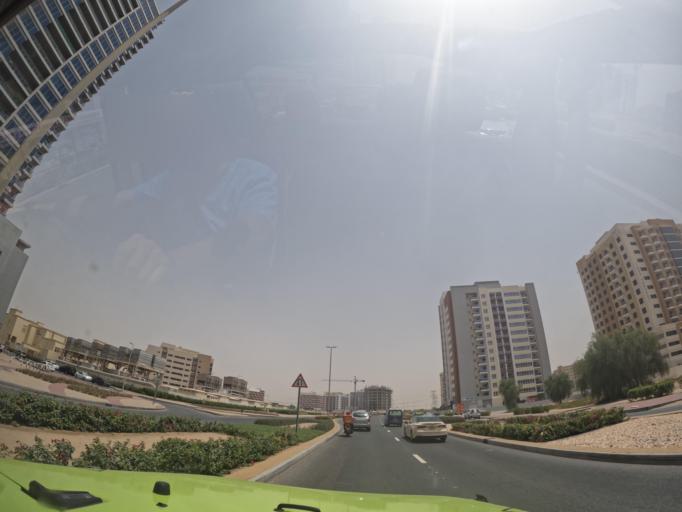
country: AE
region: Dubai
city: Dubai
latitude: 25.0898
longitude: 55.3852
